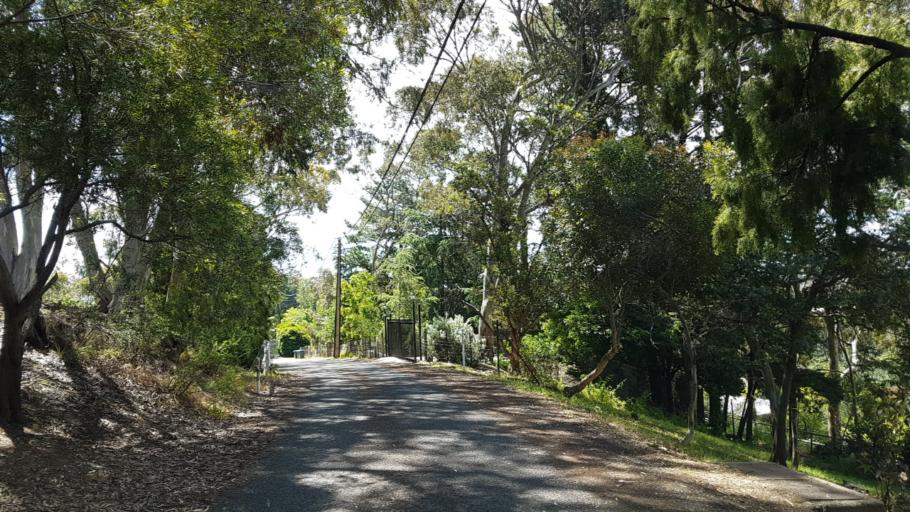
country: AU
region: South Australia
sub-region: Adelaide Hills
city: Adelaide Hills
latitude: -34.9270
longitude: 138.7282
